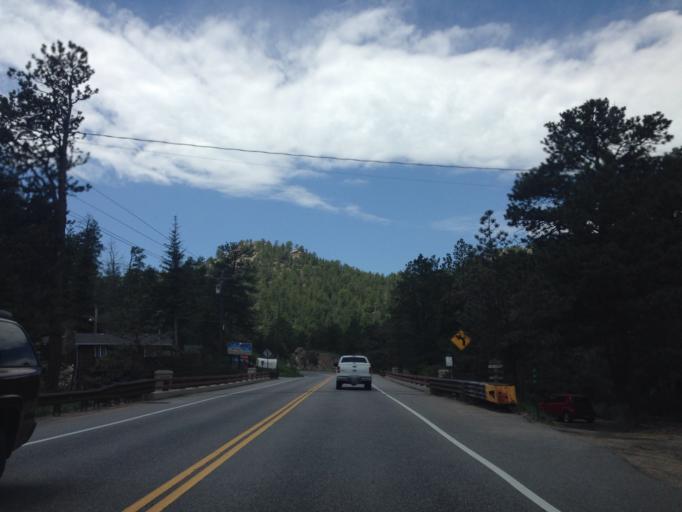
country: US
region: Colorado
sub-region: Larimer County
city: Estes Park
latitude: 40.3899
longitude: -105.4634
